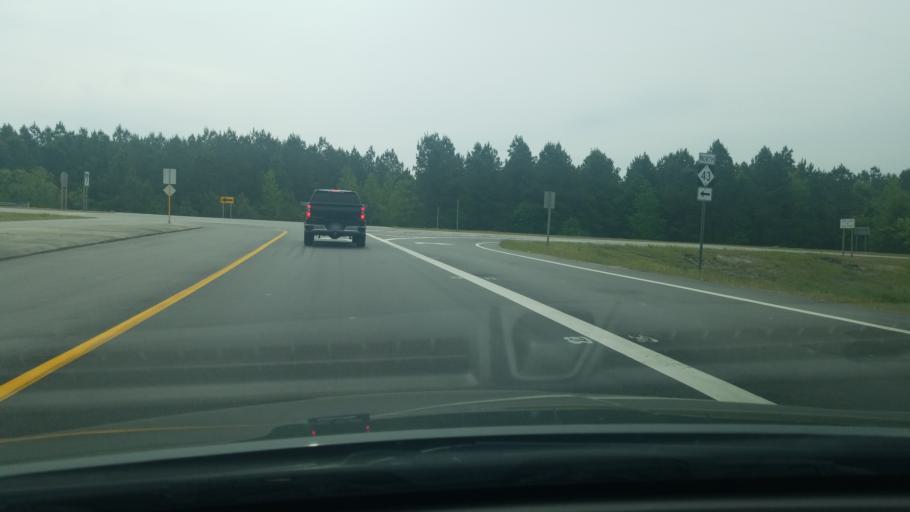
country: US
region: North Carolina
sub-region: Craven County
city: River Bend
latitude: 35.1257
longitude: -77.1356
